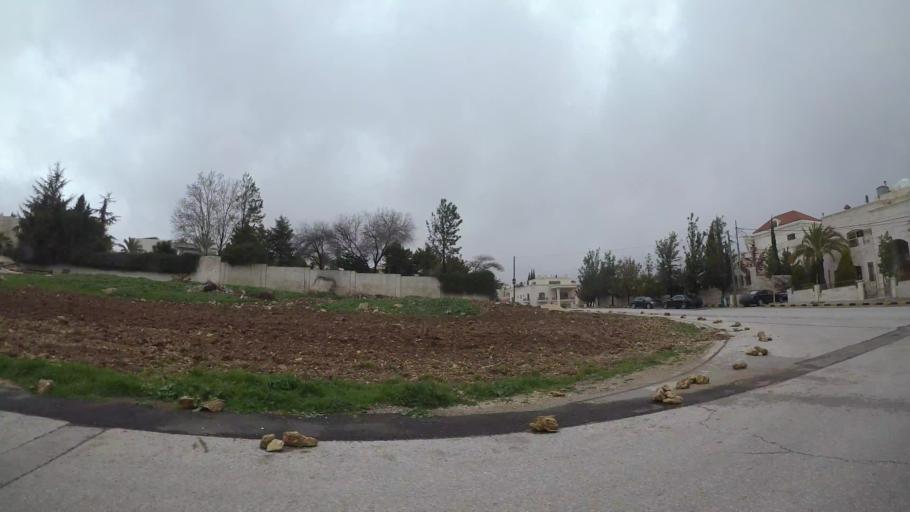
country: JO
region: Amman
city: Al Bunayyat ash Shamaliyah
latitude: 31.9371
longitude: 35.8848
